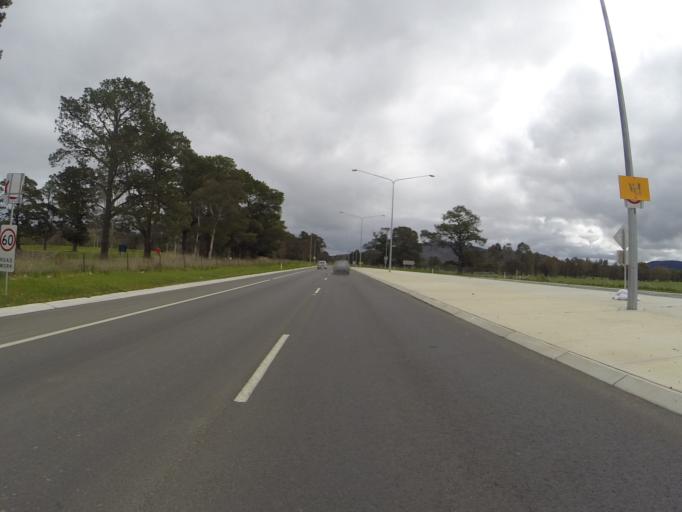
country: AU
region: Australian Capital Territory
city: Canberra
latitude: -35.2970
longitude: 149.1752
